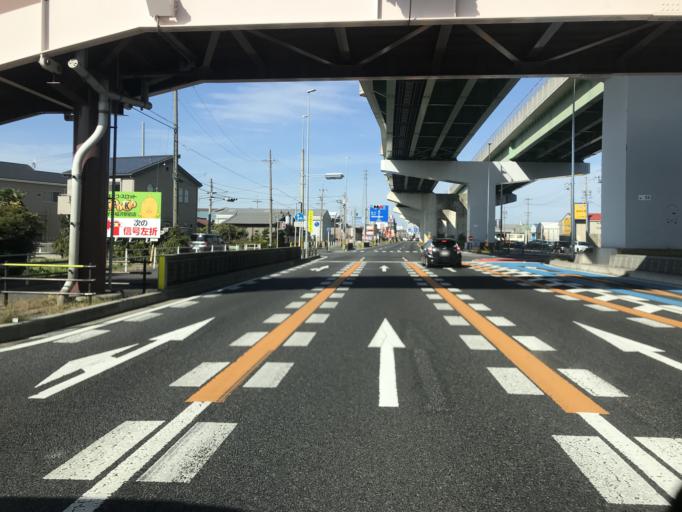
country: JP
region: Aichi
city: Iwakura
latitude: 35.2436
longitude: 136.8458
